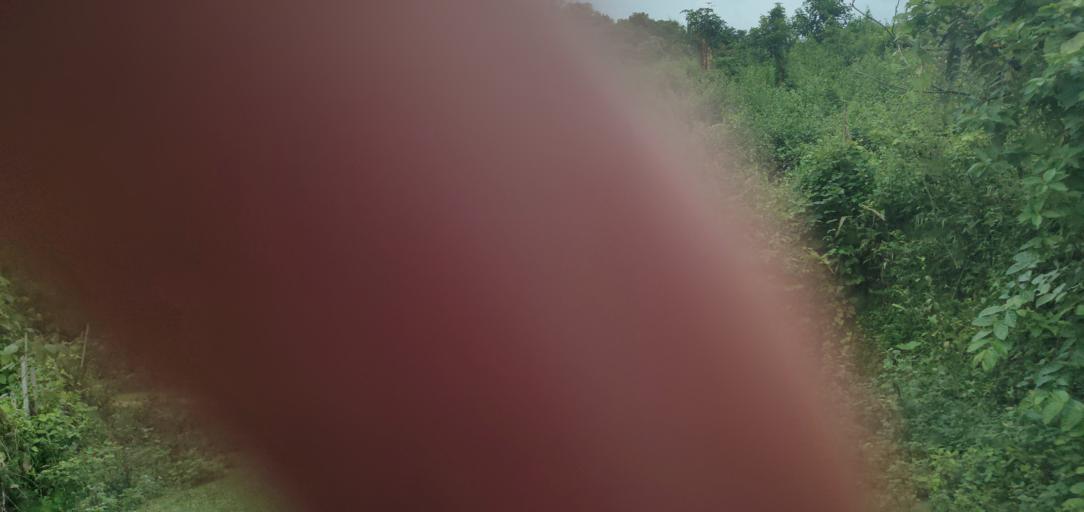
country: LA
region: Phongsali
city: Phongsali
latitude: 21.4399
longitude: 102.3306
